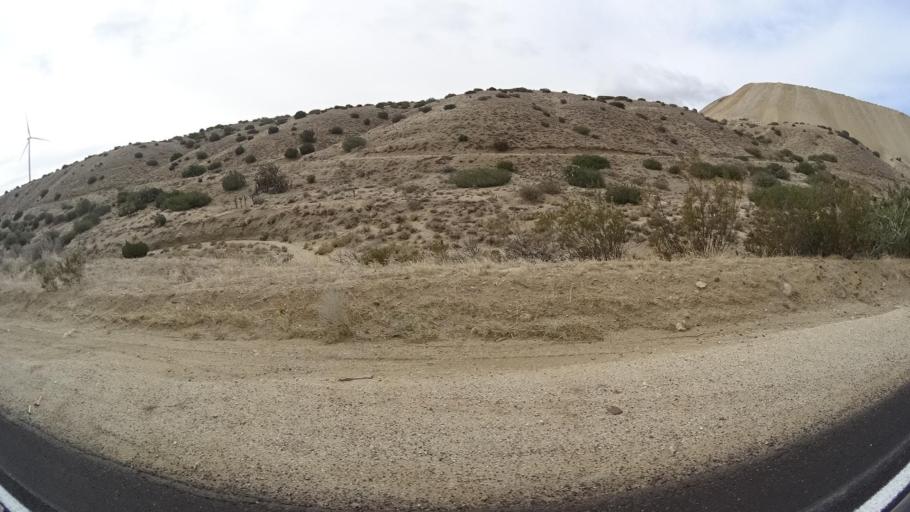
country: US
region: California
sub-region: Kern County
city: Tehachapi
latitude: 35.0494
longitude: -118.3244
